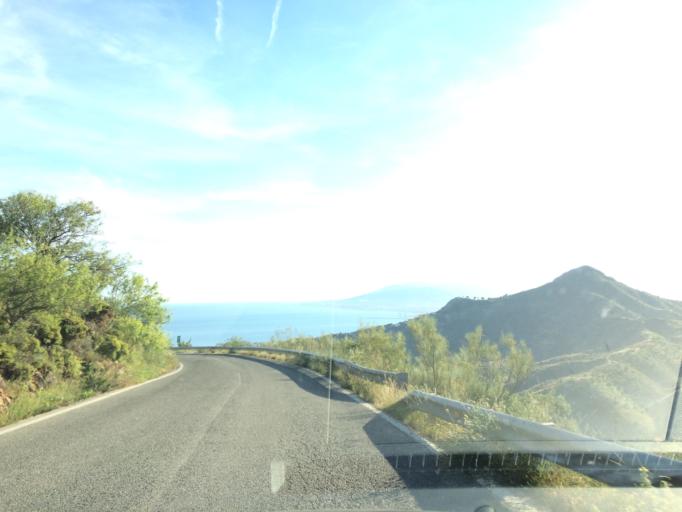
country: ES
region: Andalusia
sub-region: Provincia de Malaga
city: Totalan
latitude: 36.7531
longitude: -4.3315
